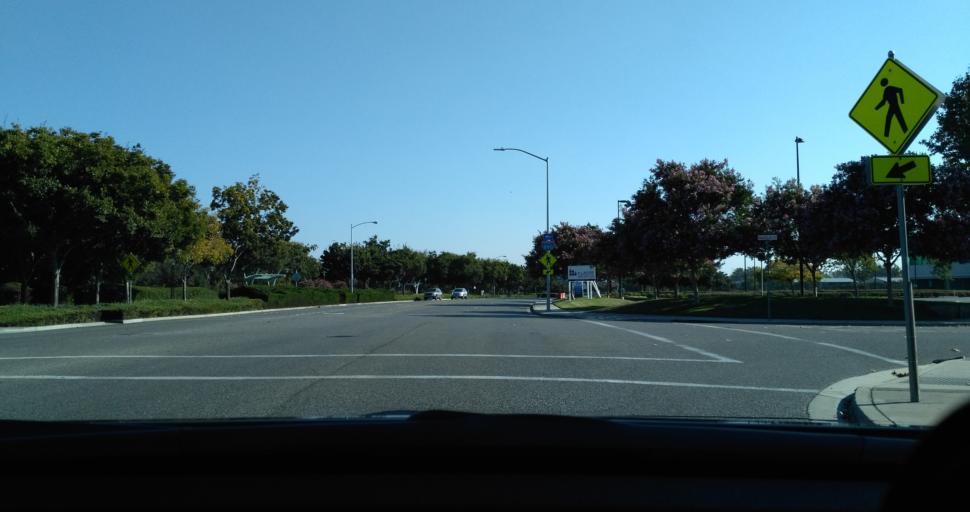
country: US
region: California
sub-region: Santa Clara County
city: Milpitas
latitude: 37.4183
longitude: -121.9208
